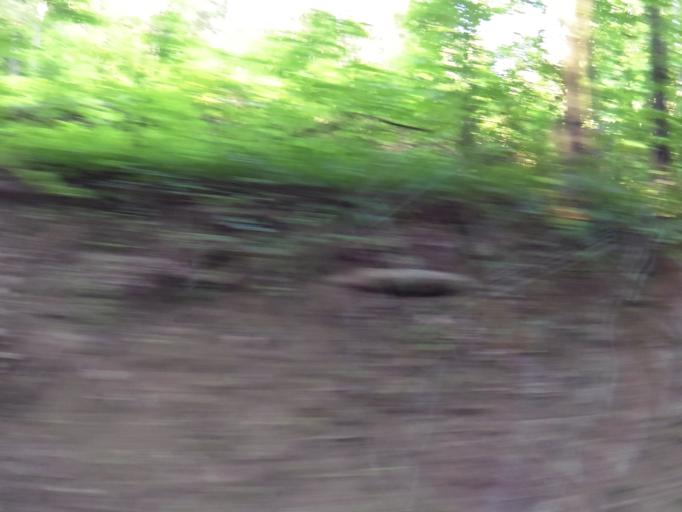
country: US
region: Tennessee
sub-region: Sevier County
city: Sevierville
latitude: 35.8540
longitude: -83.6279
